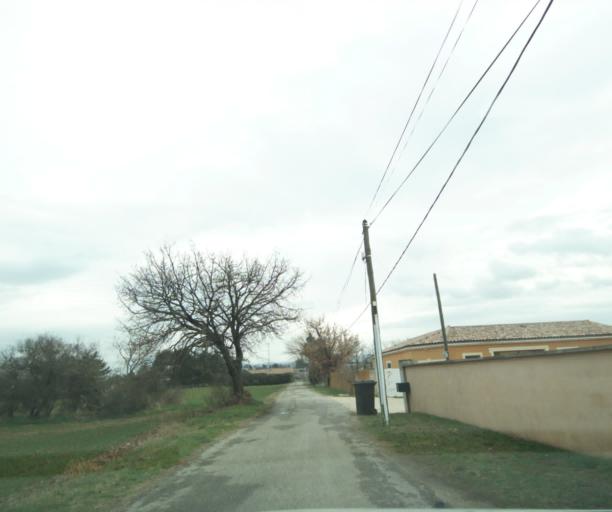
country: FR
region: Rhone-Alpes
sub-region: Departement de l'Ardeche
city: Cornas
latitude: 44.9702
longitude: 4.8798
